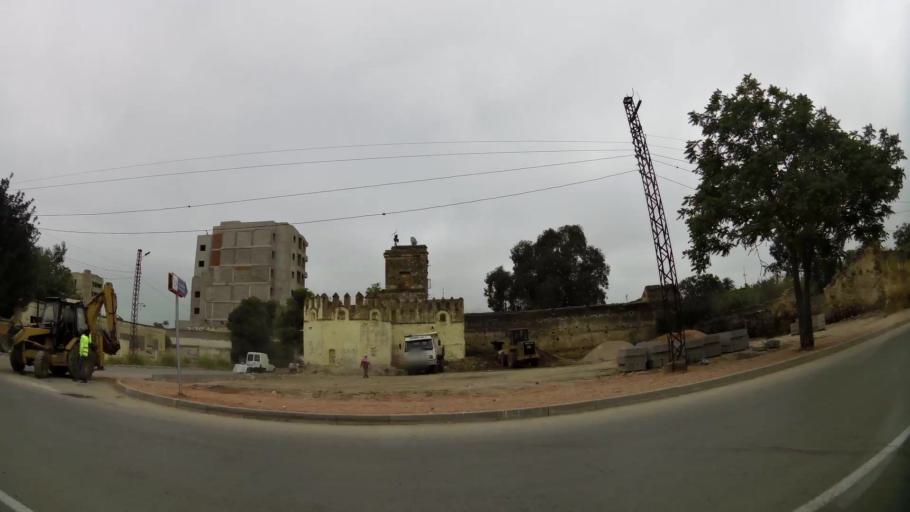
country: MA
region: Fes-Boulemane
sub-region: Fes
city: Fes
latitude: 34.0290
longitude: -5.0014
